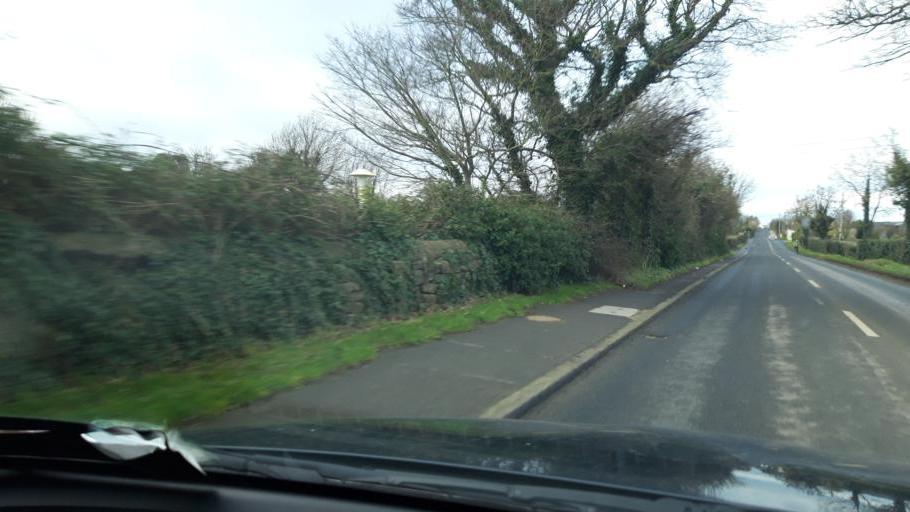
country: IE
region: Leinster
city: An Ros
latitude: 53.5410
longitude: -6.0947
